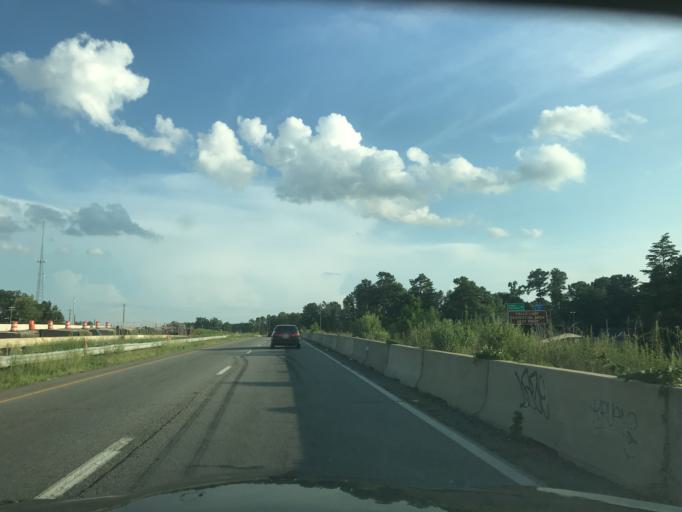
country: US
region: North Carolina
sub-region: Durham County
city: Durham
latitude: 35.9929
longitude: -78.8630
